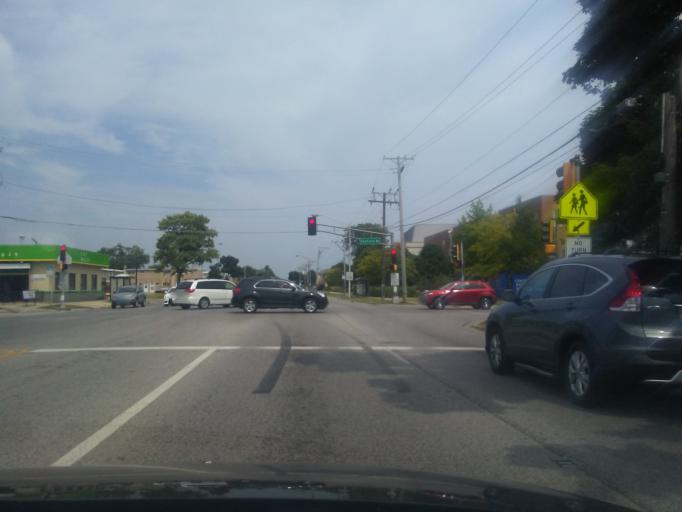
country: US
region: Illinois
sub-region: Cook County
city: Norridge
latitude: 41.9667
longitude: -87.8272
